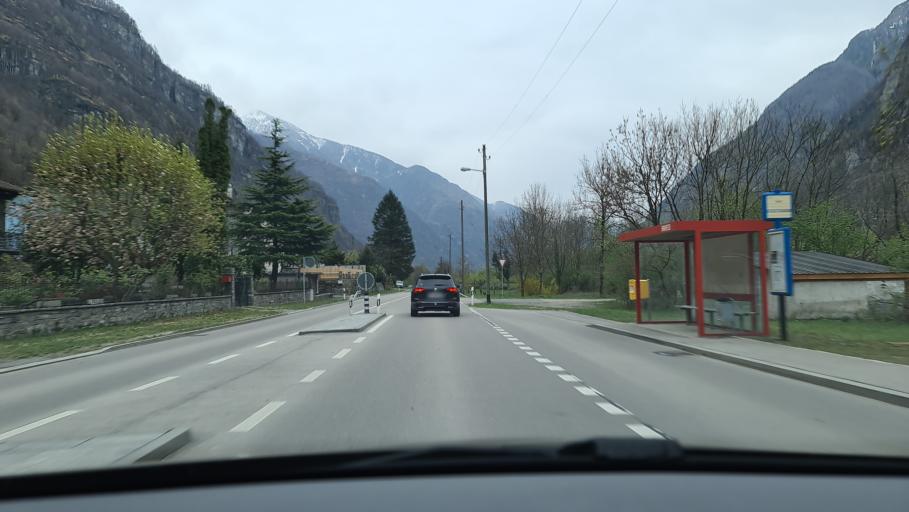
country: CH
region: Ticino
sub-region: Vallemaggia District
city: Cevio
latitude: 46.2968
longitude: 8.6300
